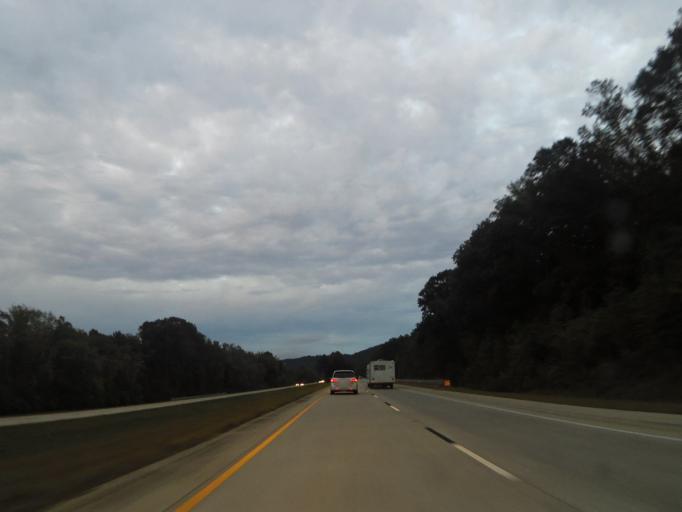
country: US
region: Alabama
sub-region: Etowah County
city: Attalla
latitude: 34.0457
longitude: -86.0563
